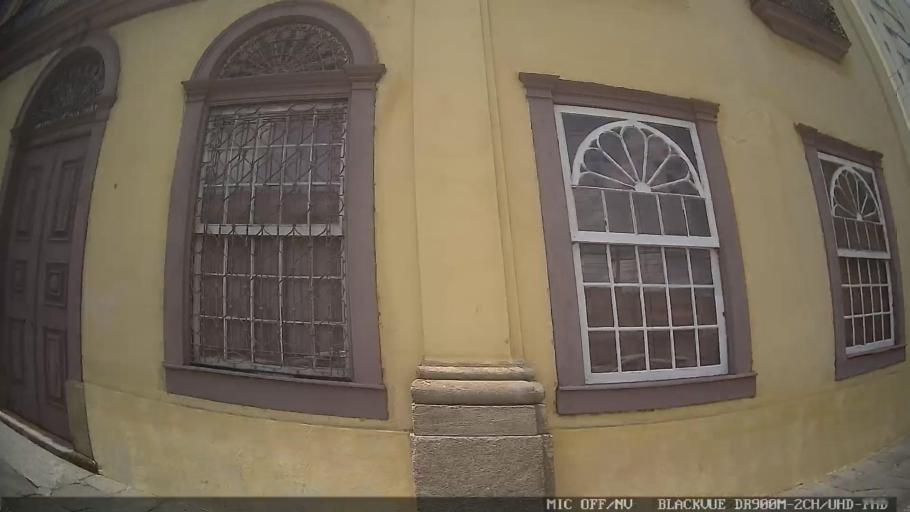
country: BR
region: Sao Paulo
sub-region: Jacarei
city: Jacarei
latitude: -23.3063
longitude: -45.9728
